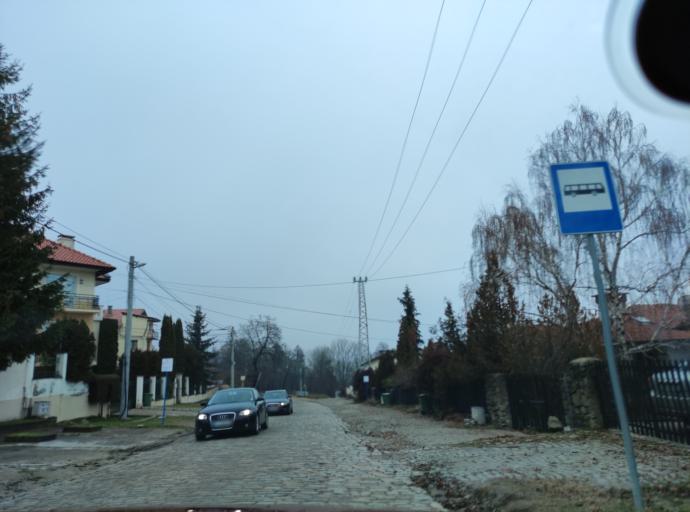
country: BG
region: Sofia-Capital
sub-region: Stolichna Obshtina
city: Sofia
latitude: 42.6248
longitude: 23.3086
